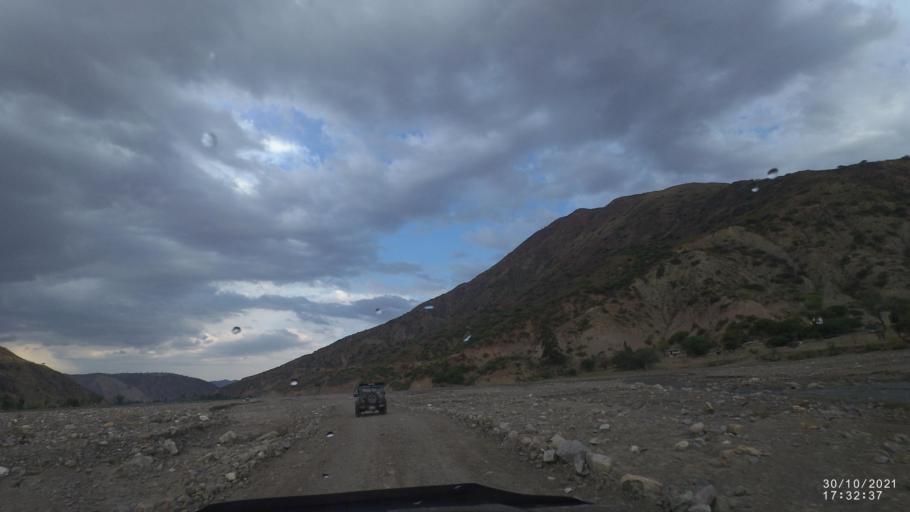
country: BO
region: Cochabamba
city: Sipe Sipe
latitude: -17.5260
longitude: -66.5862
